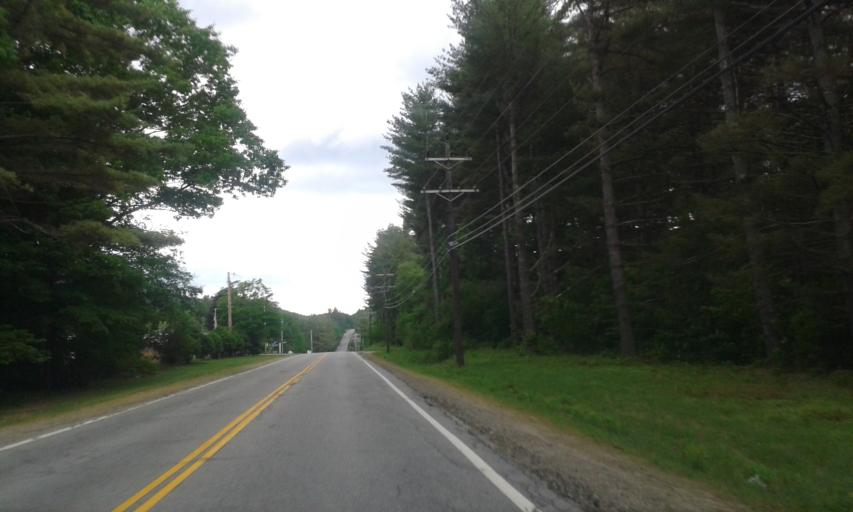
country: US
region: New Hampshire
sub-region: Grafton County
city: Woodstock
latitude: 44.0087
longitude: -71.6859
